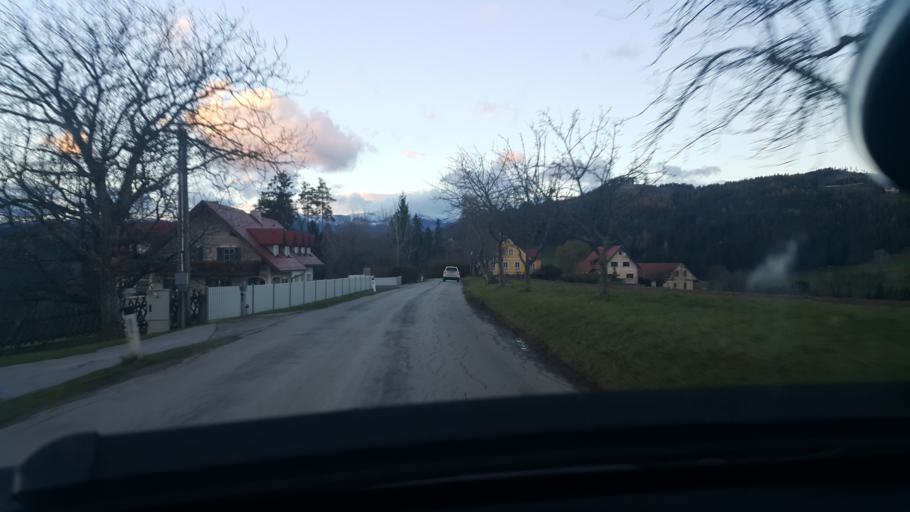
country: AT
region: Styria
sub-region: Politischer Bezirk Graz-Umgebung
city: Stiwoll
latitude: 47.1087
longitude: 15.2255
